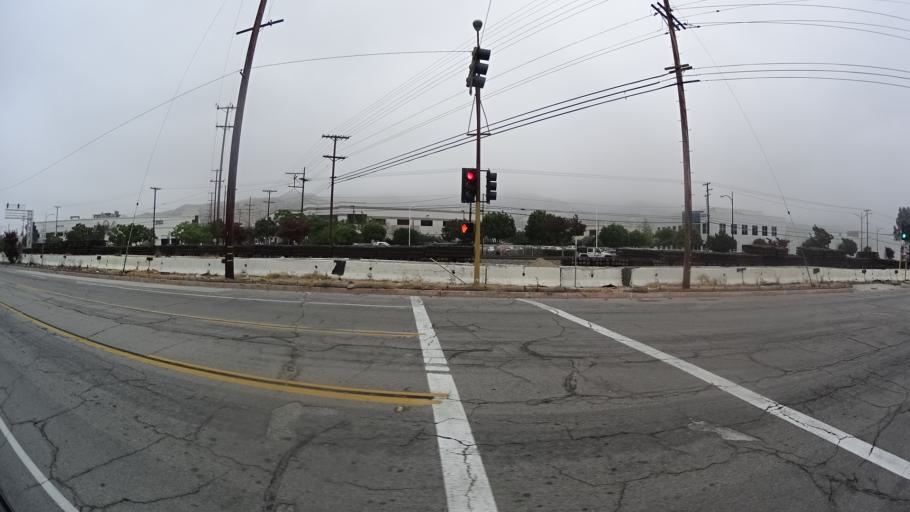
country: US
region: California
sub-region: Los Angeles County
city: Burbank
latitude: 34.2023
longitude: -118.3445
